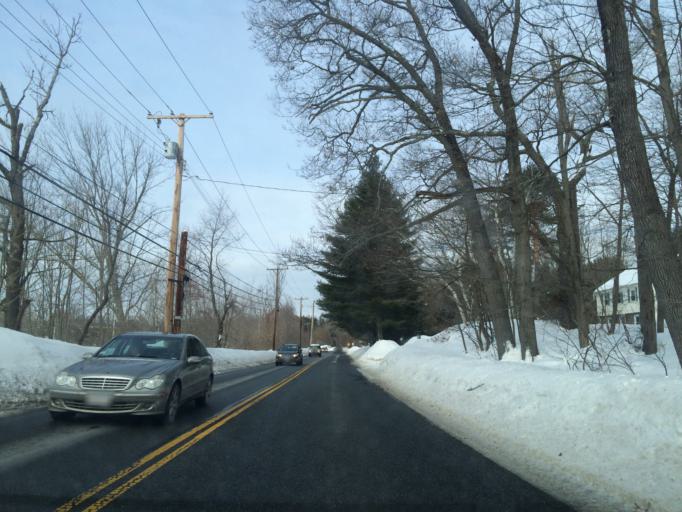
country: US
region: Massachusetts
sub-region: Middlesex County
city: Weston
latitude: 42.3420
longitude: -71.3021
